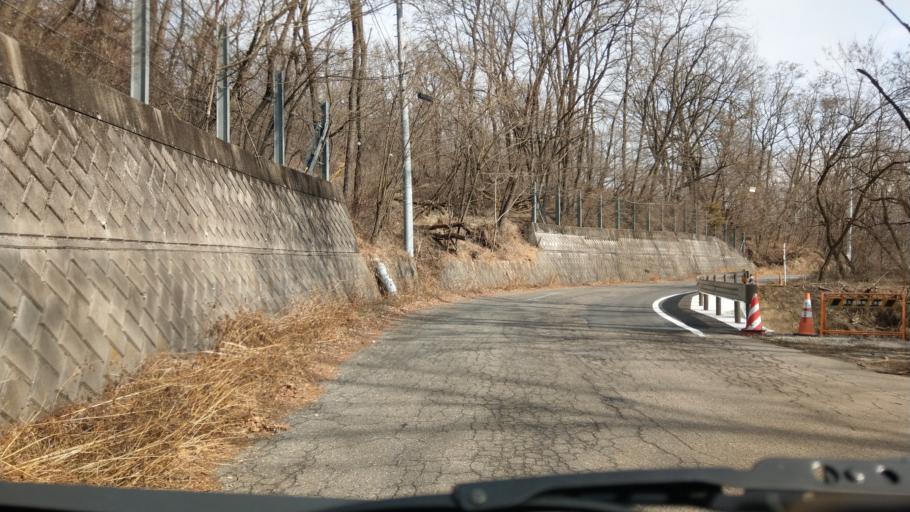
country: JP
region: Nagano
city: Komoro
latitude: 36.2862
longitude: 138.4079
